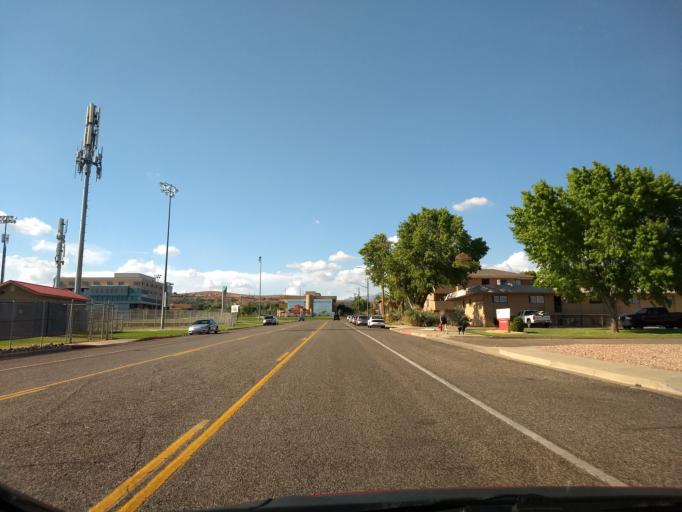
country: US
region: Utah
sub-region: Washington County
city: Saint George
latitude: 37.0994
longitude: -113.5643
